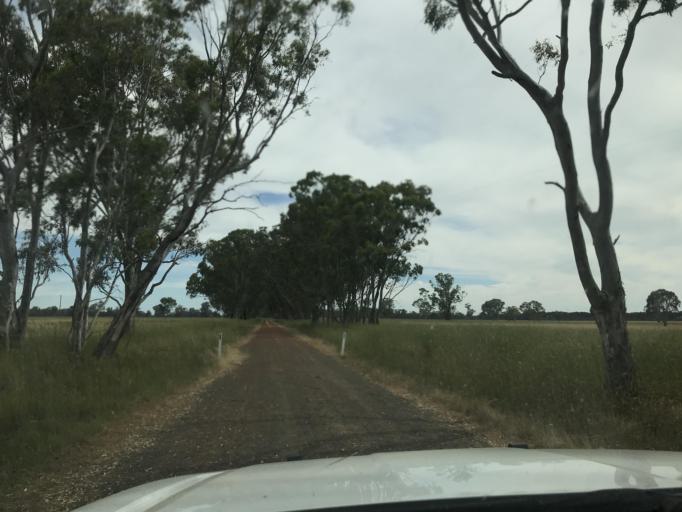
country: AU
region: South Australia
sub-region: Naracoorte and Lucindale
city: Naracoorte
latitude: -36.9890
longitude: 141.4693
